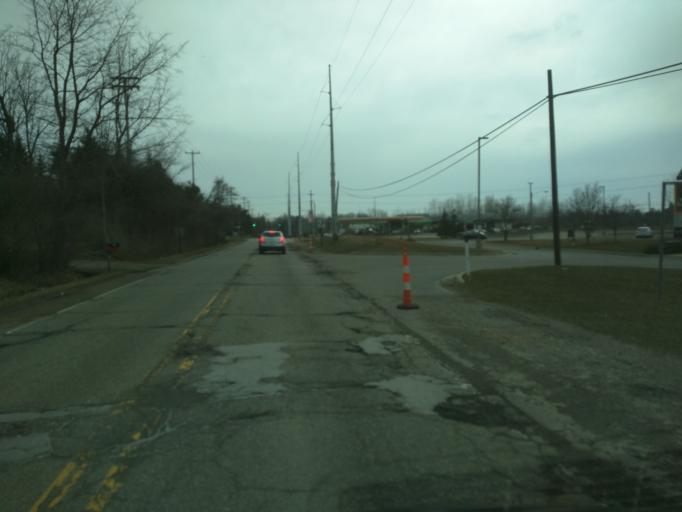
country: US
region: Michigan
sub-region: Eaton County
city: Waverly
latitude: 42.7149
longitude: -84.6014
